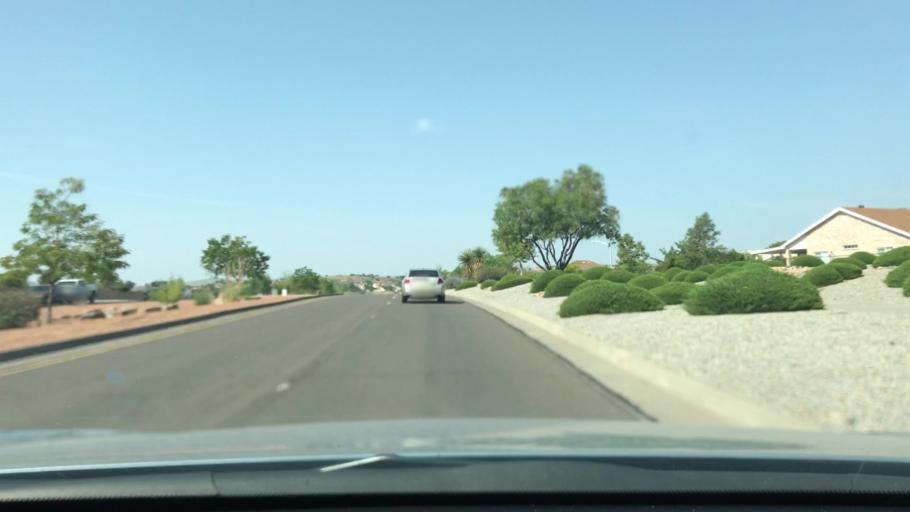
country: US
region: New Mexico
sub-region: Bernalillo County
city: Paradise Hills
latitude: 35.1809
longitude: -106.6834
